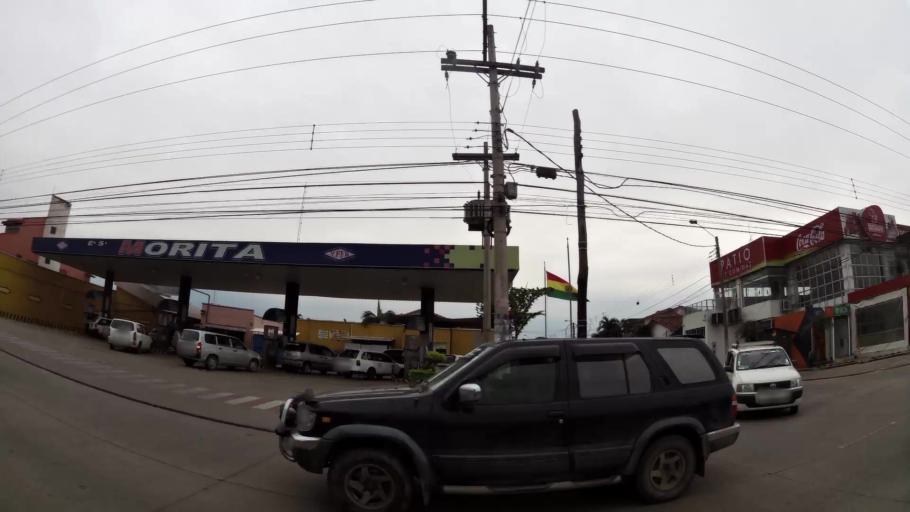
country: BO
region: Santa Cruz
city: Santa Cruz de la Sierra
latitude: -17.8208
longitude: -63.1841
